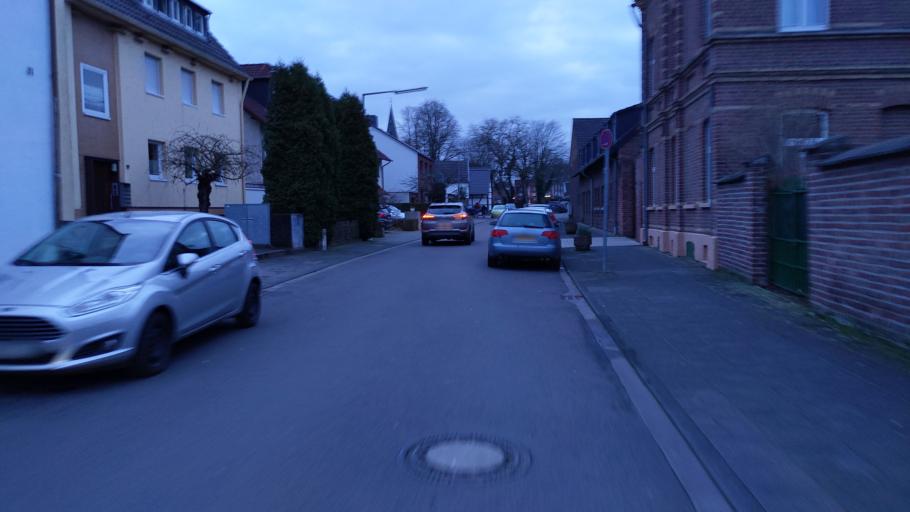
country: DE
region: North Rhine-Westphalia
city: Monheim am Rhein
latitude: 51.0366
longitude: 6.9061
